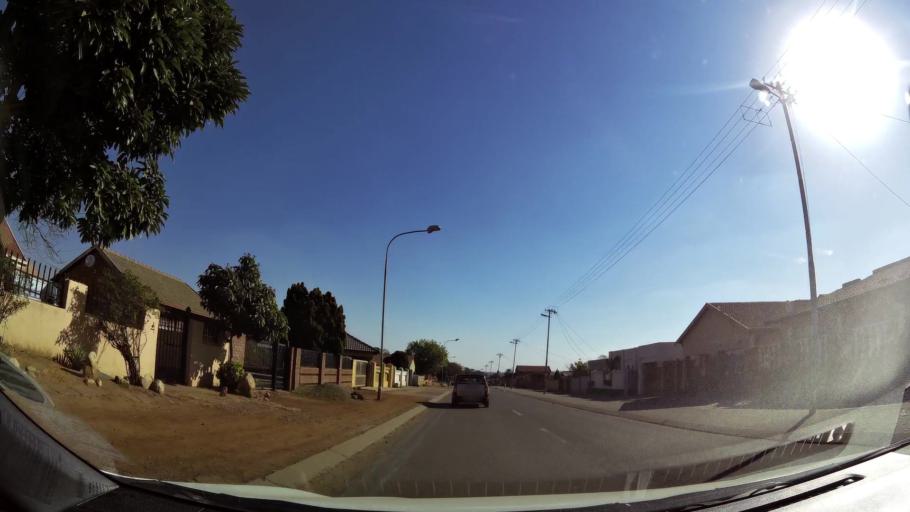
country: ZA
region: Gauteng
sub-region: City of Tshwane Metropolitan Municipality
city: Cullinan
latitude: -25.7121
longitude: 28.3886
